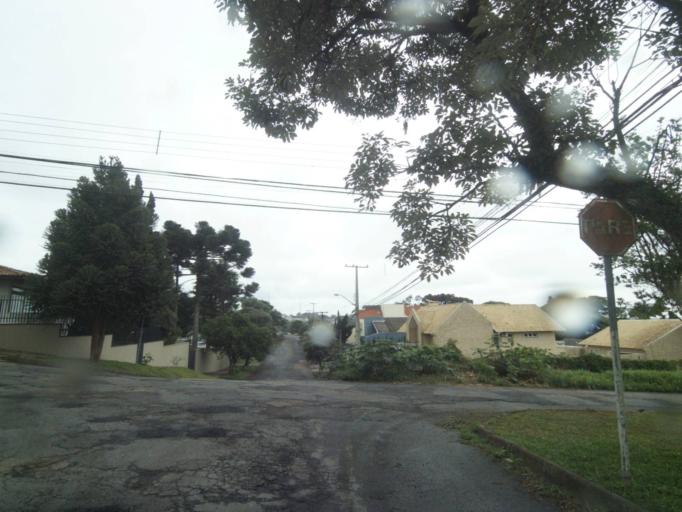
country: BR
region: Parana
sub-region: Curitiba
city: Curitiba
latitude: -25.4112
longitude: -49.2898
